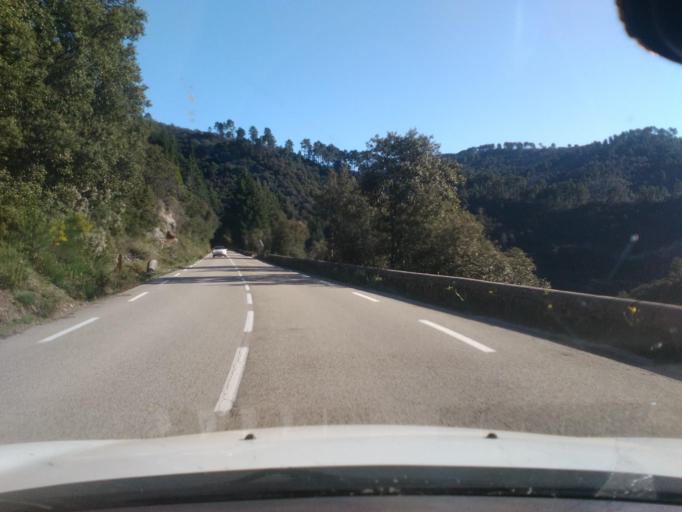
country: FR
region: Languedoc-Roussillon
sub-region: Departement du Gard
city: Lasalle
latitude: 44.1052
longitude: 3.8100
